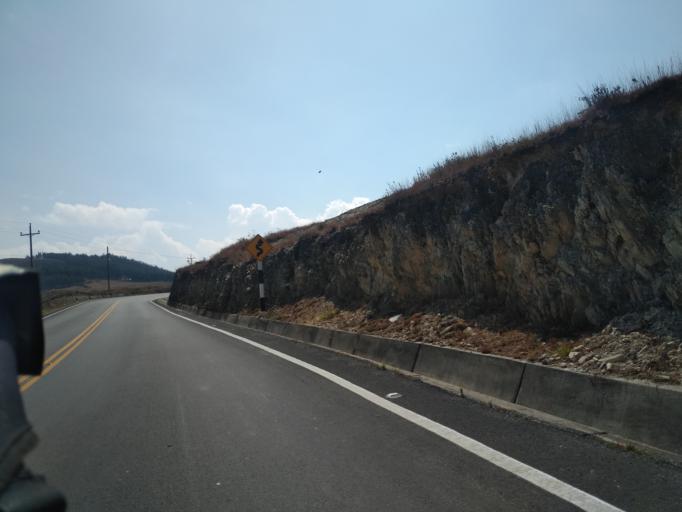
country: PE
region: Cajamarca
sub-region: Provincia de Cajamarca
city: Llacanora
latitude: -7.2065
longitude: -78.3850
